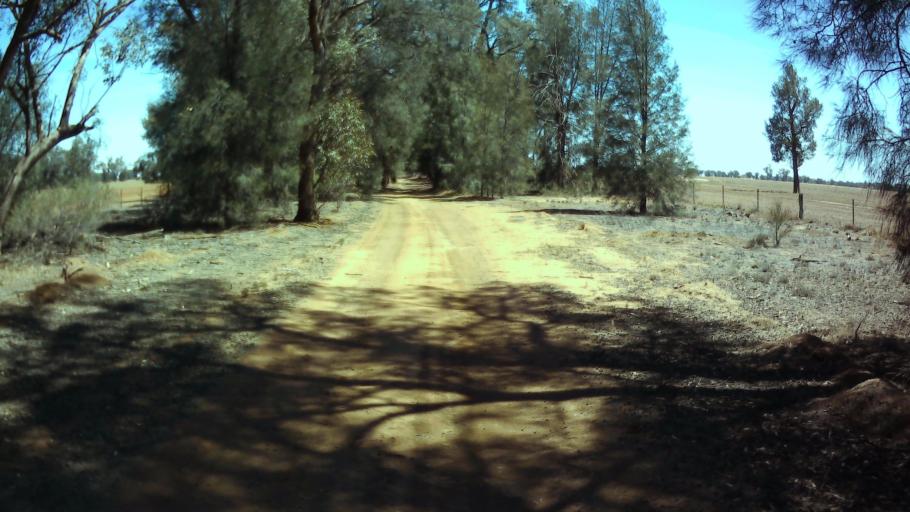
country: AU
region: New South Wales
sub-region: Bland
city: West Wyalong
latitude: -33.9196
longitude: 147.6829
